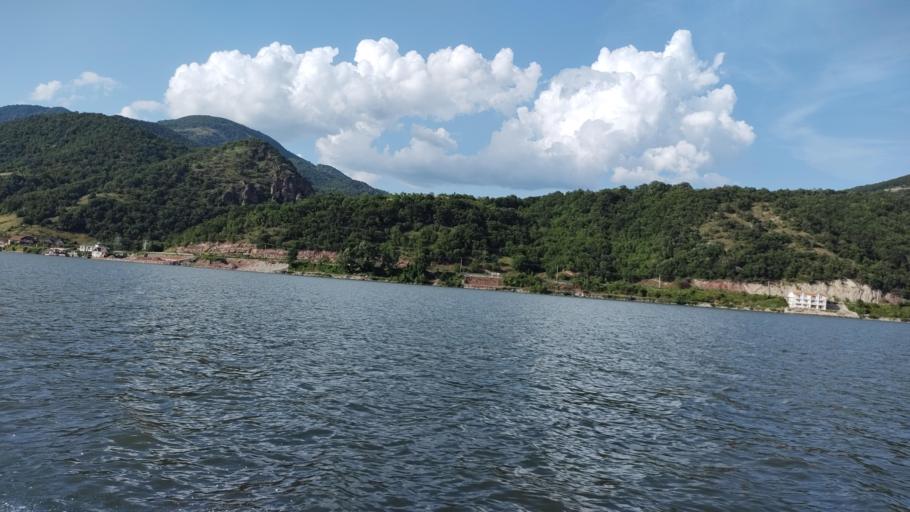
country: RO
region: Mehedinti
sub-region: Comuna Svinita
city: Svinita
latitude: 44.5338
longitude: 22.0641
